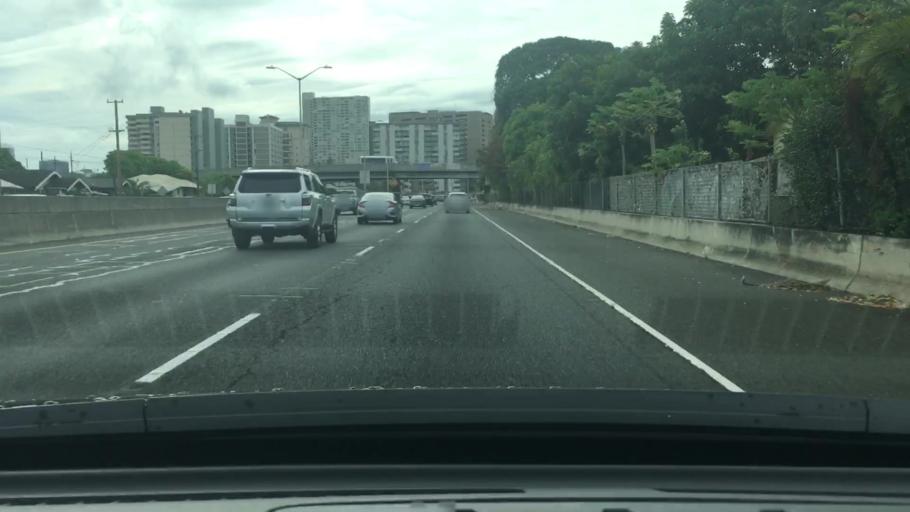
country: US
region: Hawaii
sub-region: Honolulu County
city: Honolulu
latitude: 21.2977
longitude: -157.8276
